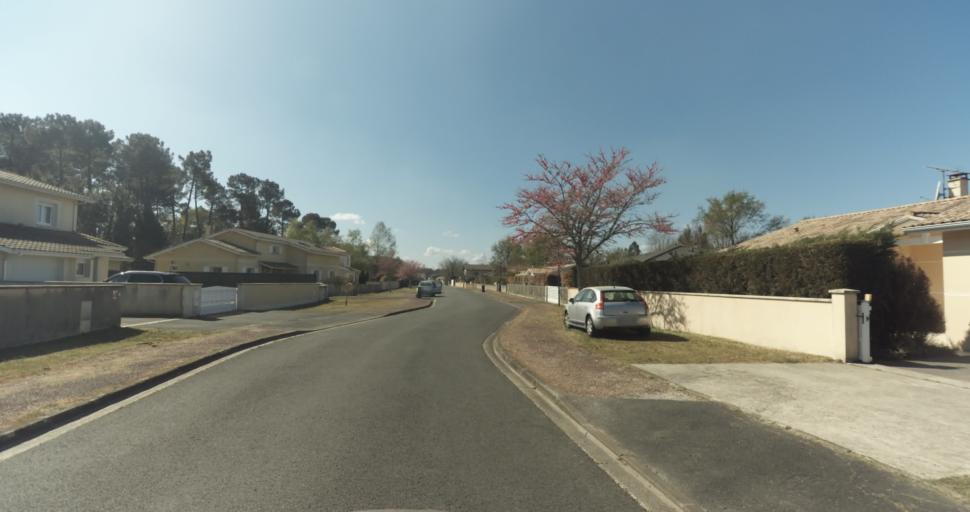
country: FR
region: Aquitaine
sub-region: Departement de la Gironde
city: Martignas-sur-Jalle
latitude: 44.7991
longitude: -0.7856
